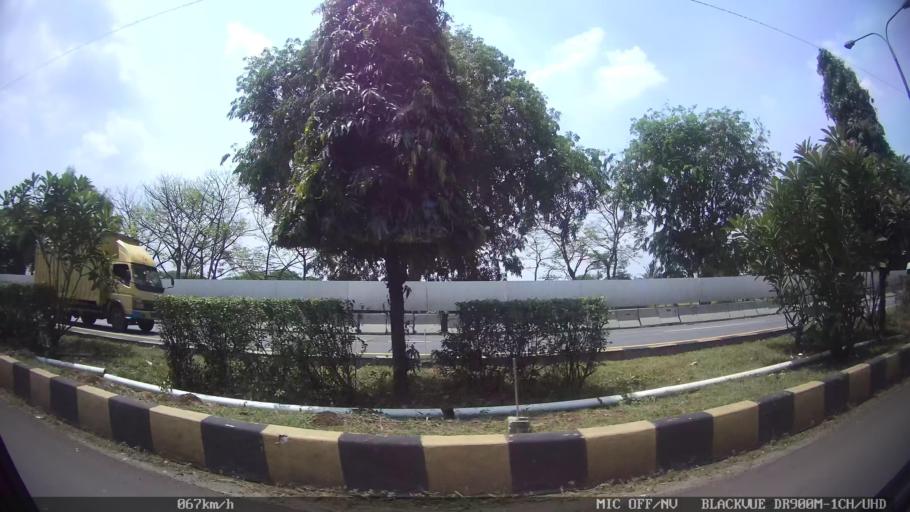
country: ID
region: Banten
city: Serang
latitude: -6.1309
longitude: 106.2006
